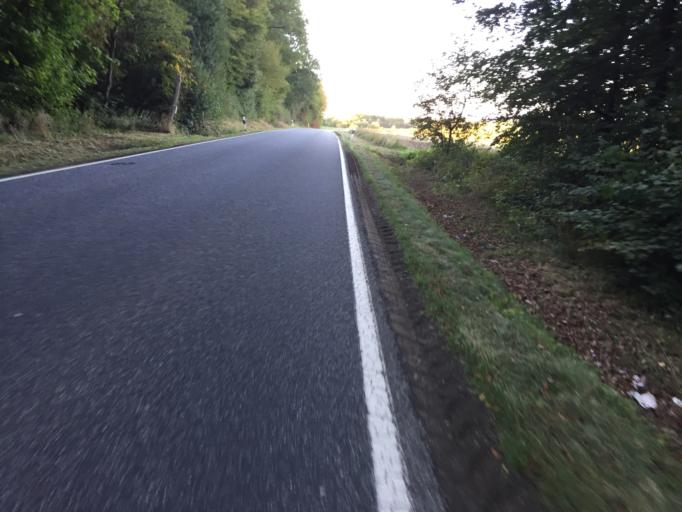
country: DE
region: Hesse
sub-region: Regierungsbezirk Giessen
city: Lich
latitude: 50.5175
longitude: 8.7604
